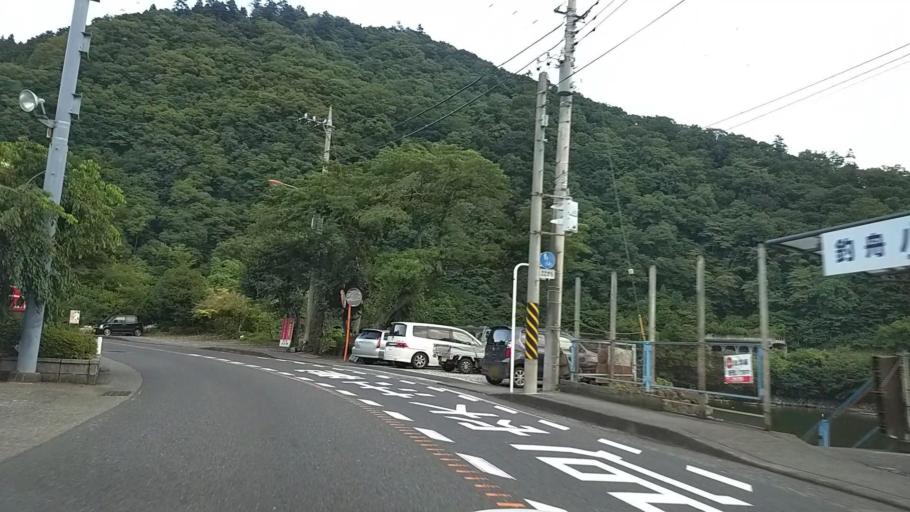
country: JP
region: Yamanashi
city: Uenohara
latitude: 35.6125
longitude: 139.1929
